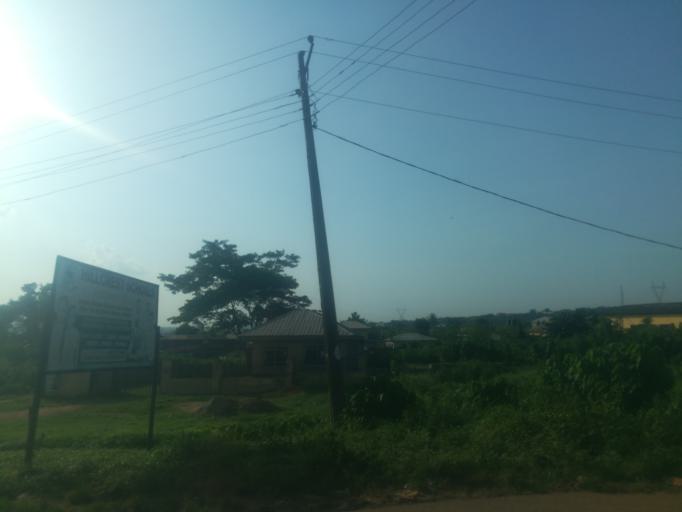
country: NG
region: Oyo
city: Moniya
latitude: 7.5156
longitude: 3.9143
